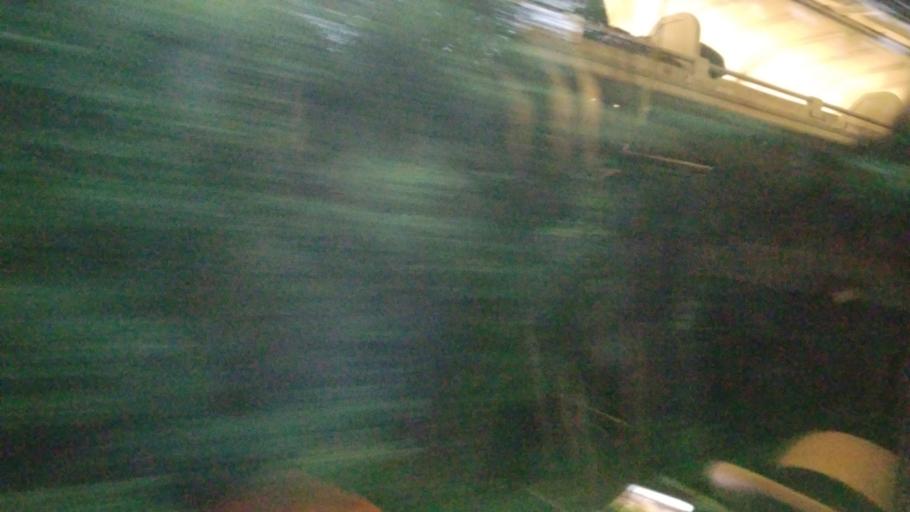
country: US
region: Virginia
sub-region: Orange County
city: Orange
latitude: 38.2374
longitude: -78.1380
